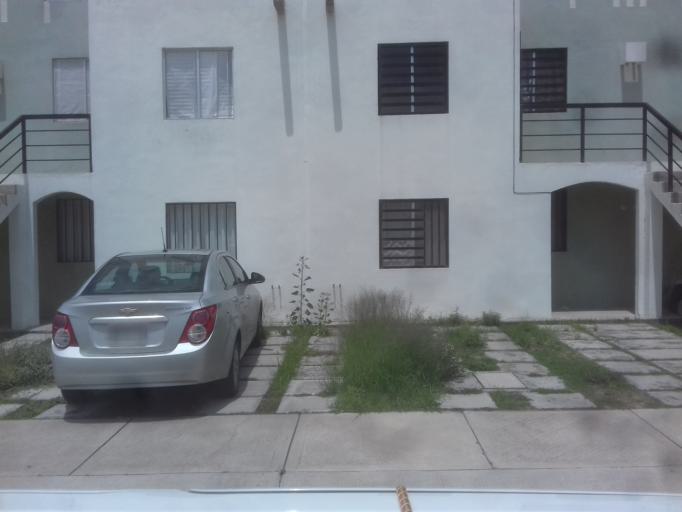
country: MX
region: Aguascalientes
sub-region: Aguascalientes
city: San Sebastian [Fraccionamiento]
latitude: 21.8067
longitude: -102.2699
